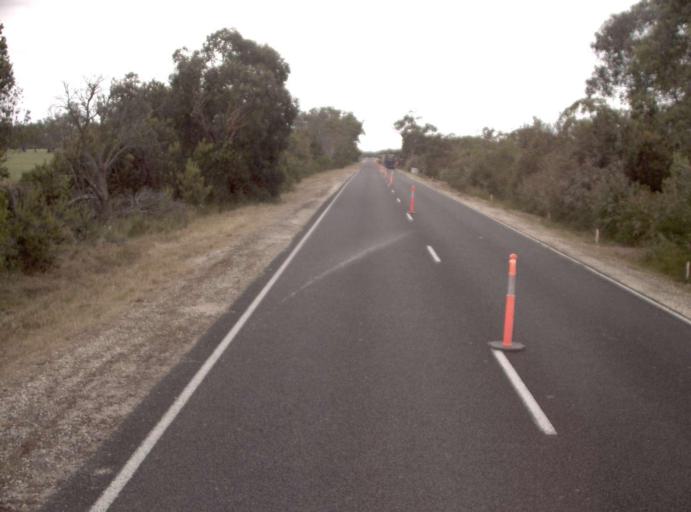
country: AU
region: Victoria
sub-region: Wellington
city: Sale
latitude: -38.1299
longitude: 147.4254
